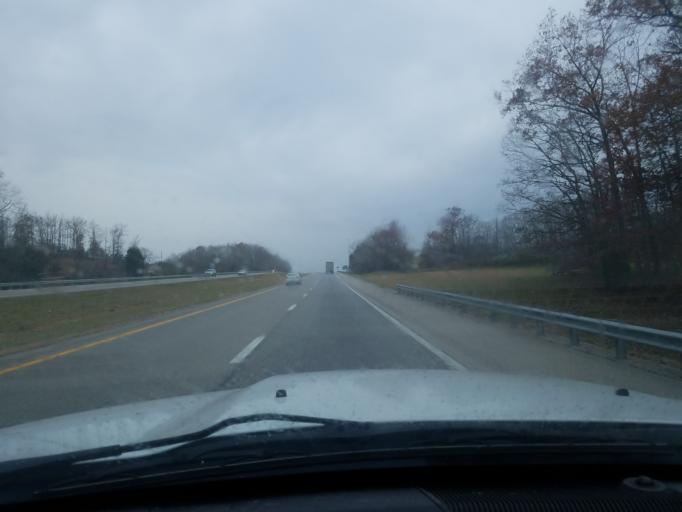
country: US
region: Kentucky
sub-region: Rowan County
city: Morehead
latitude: 38.1856
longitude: -83.5437
